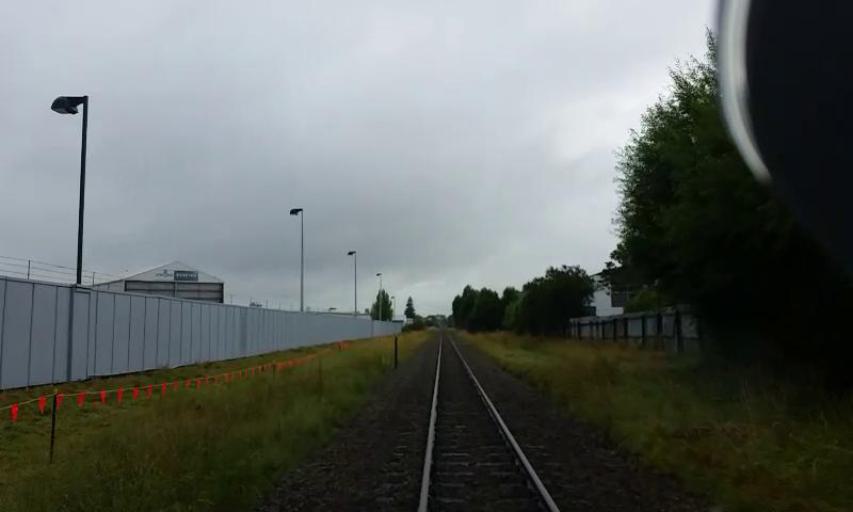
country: NZ
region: Canterbury
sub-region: Christchurch City
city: Christchurch
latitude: -43.5353
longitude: 172.6095
